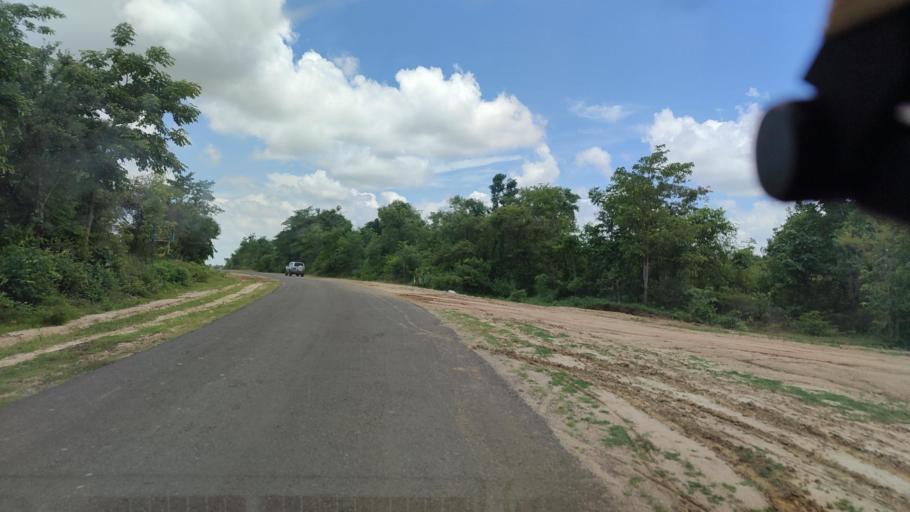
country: MM
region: Magway
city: Taungdwingyi
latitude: 20.1542
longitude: 95.5794
